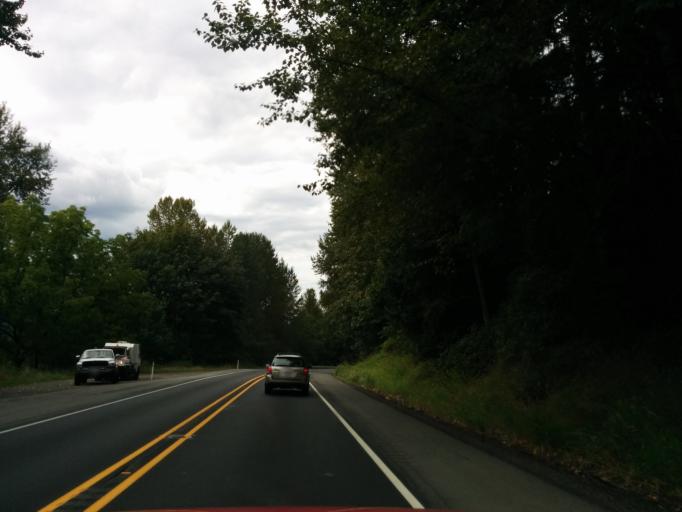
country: US
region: Washington
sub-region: King County
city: Duvall
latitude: 47.7803
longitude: -121.9648
